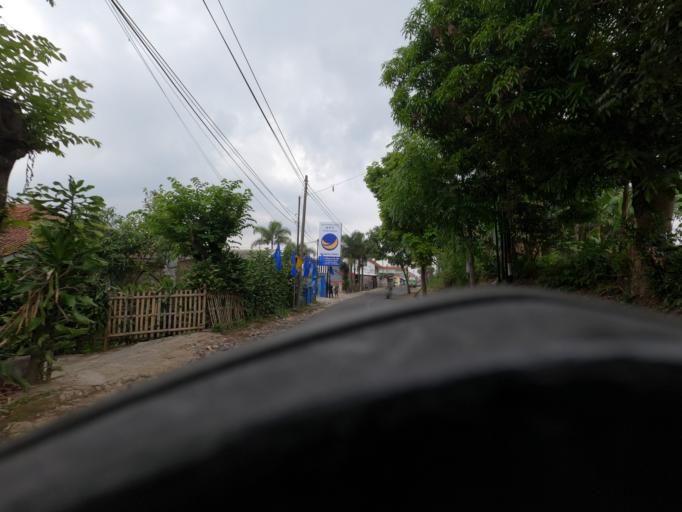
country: ID
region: West Java
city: Lembang
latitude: -6.8054
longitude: 107.5701
